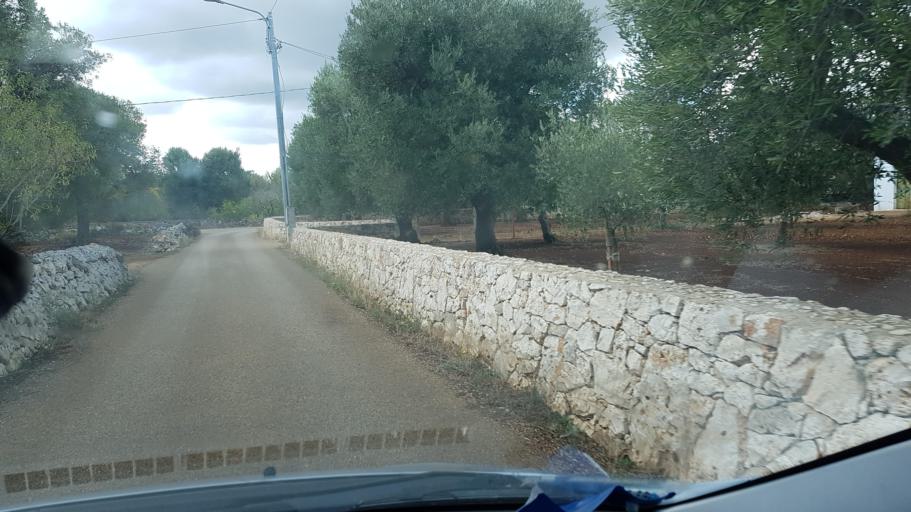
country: IT
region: Apulia
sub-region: Provincia di Brindisi
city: San Vito dei Normanni
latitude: 40.6524
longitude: 17.7283
